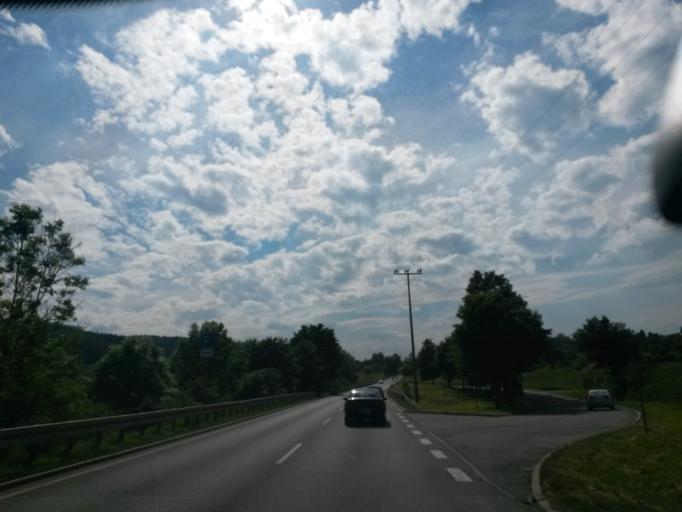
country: DE
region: Baden-Wuerttemberg
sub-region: Regierungsbezirk Stuttgart
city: Weil der Stadt
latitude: 48.7467
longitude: 8.8520
